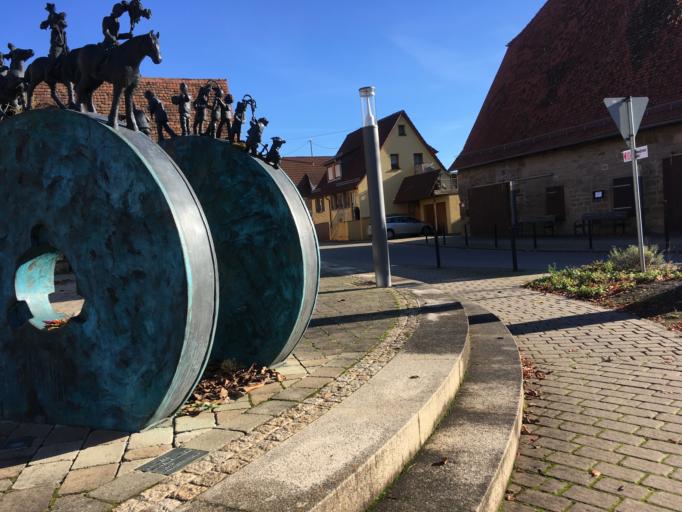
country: DE
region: Baden-Wuerttemberg
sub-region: Karlsruhe Region
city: Oberderdingen
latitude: 49.0693
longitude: 8.8064
